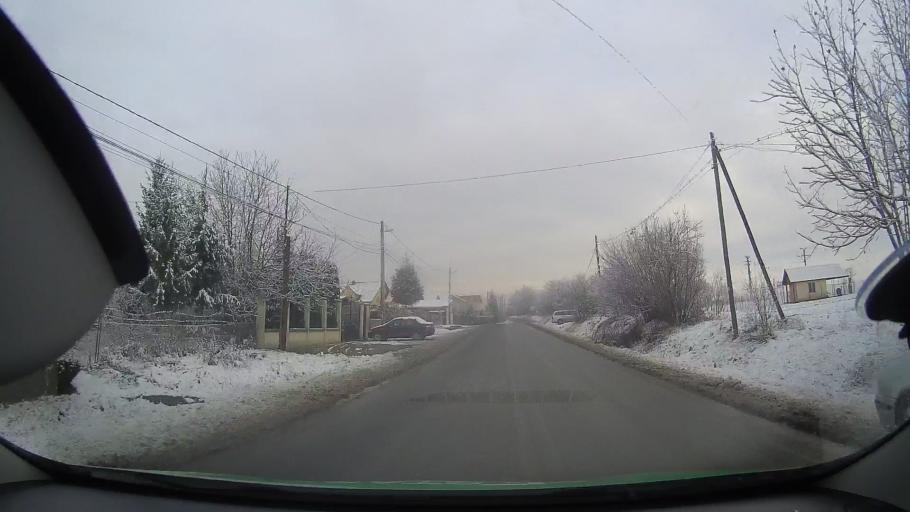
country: RO
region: Mures
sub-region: Comuna Bogata
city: Bogata
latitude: 46.4602
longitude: 24.0792
